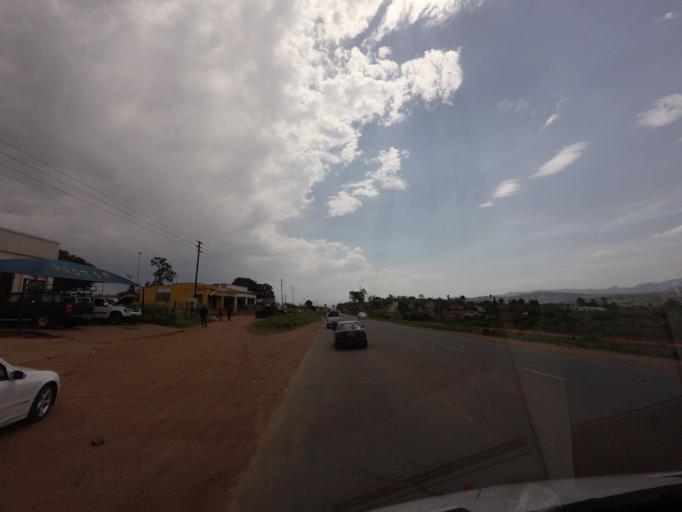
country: SZ
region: Manzini
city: Manzini
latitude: -26.4925
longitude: 31.4084
